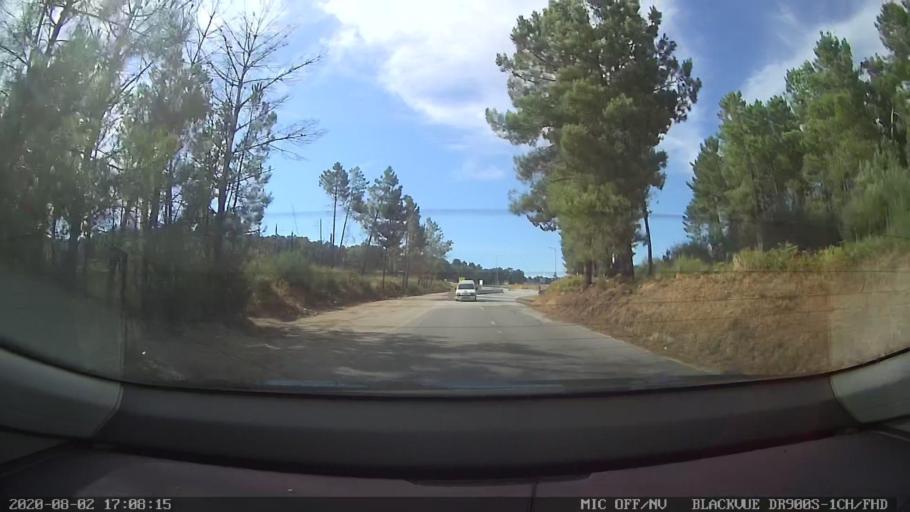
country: PT
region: Vila Real
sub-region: Sabrosa
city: Sabrosa
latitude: 41.3487
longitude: -7.5979
